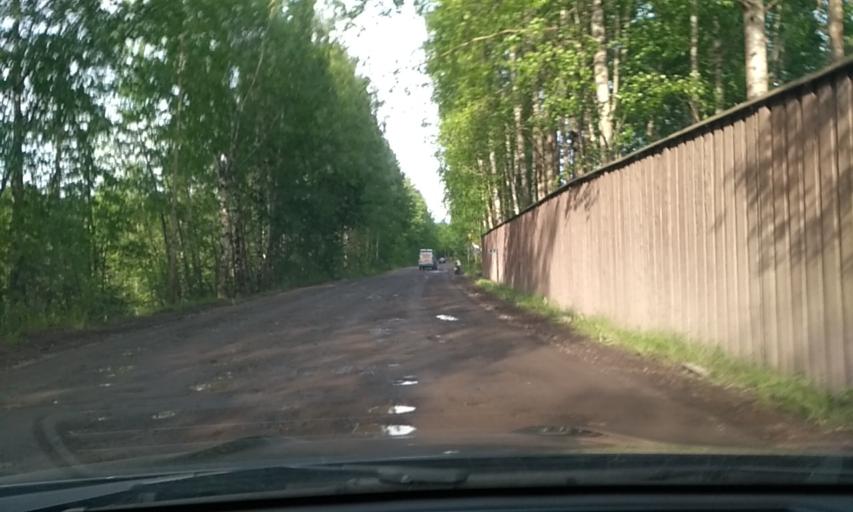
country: RU
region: Leningrad
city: Otradnoye
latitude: 59.7869
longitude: 30.7792
